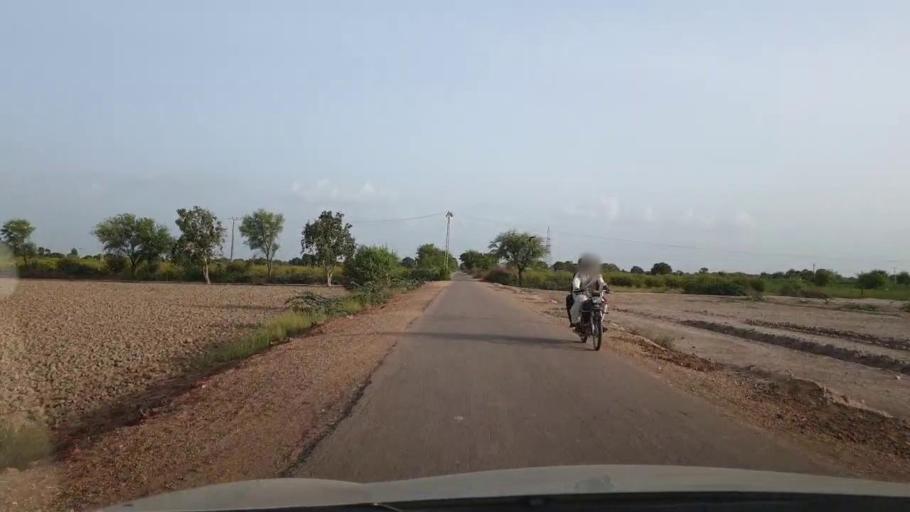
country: PK
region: Sindh
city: Tando Ghulam Ali
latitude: 25.1148
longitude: 68.8849
